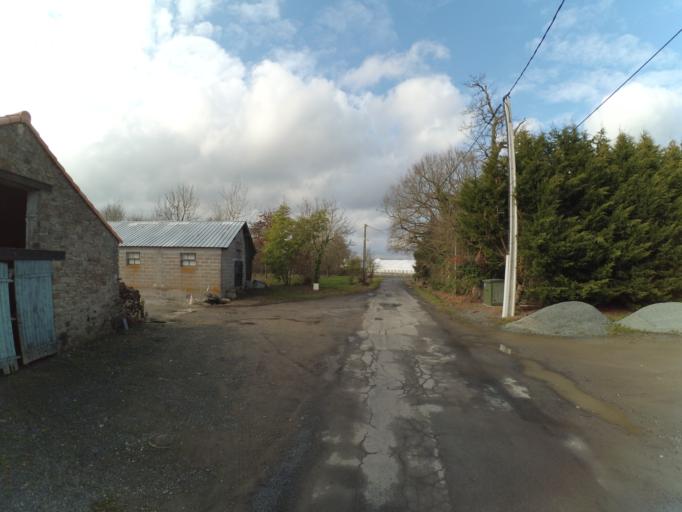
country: FR
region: Pays de la Loire
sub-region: Departement de la Loire-Atlantique
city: Clisson
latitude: 47.0753
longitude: -1.2794
